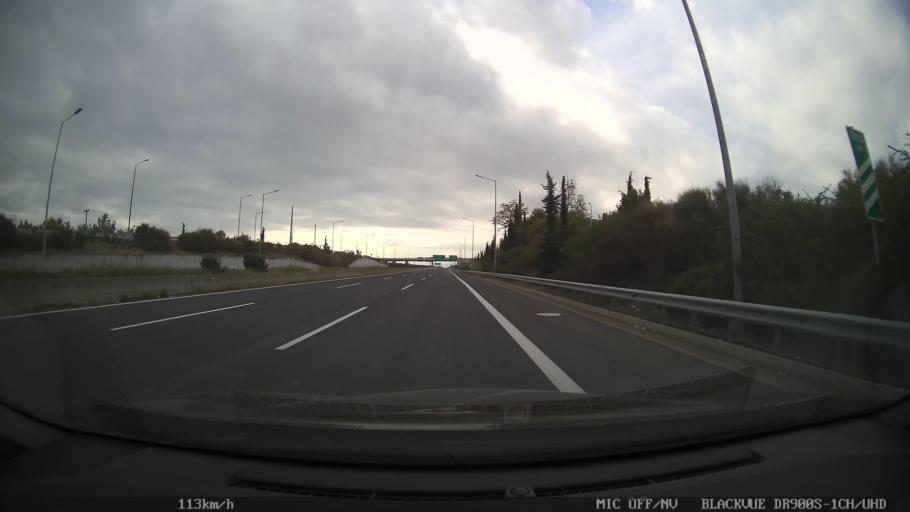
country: GR
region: Central Macedonia
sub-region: Nomos Pierias
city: Litochoro
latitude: 40.1356
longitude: 22.5449
